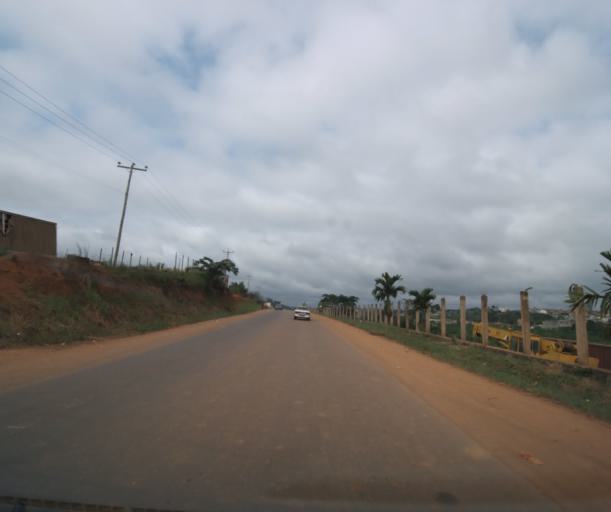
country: CM
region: Centre
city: Yaounde
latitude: 3.8055
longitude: 11.5131
